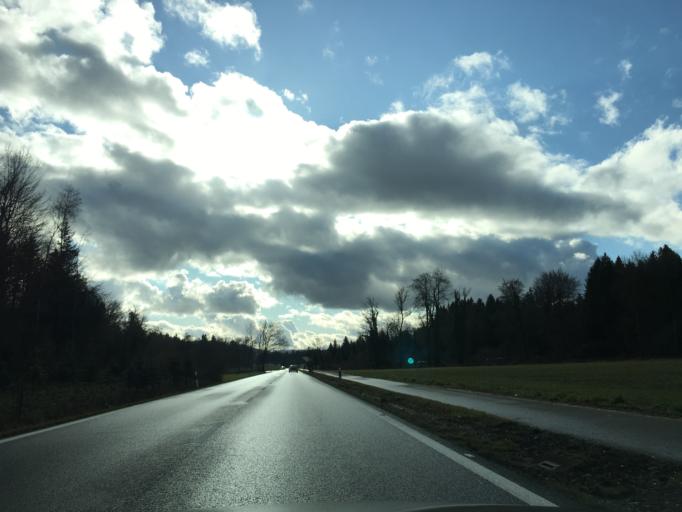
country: CH
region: Aargau
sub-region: Bezirk Muri
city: Oberruti
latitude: 47.1742
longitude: 8.3944
